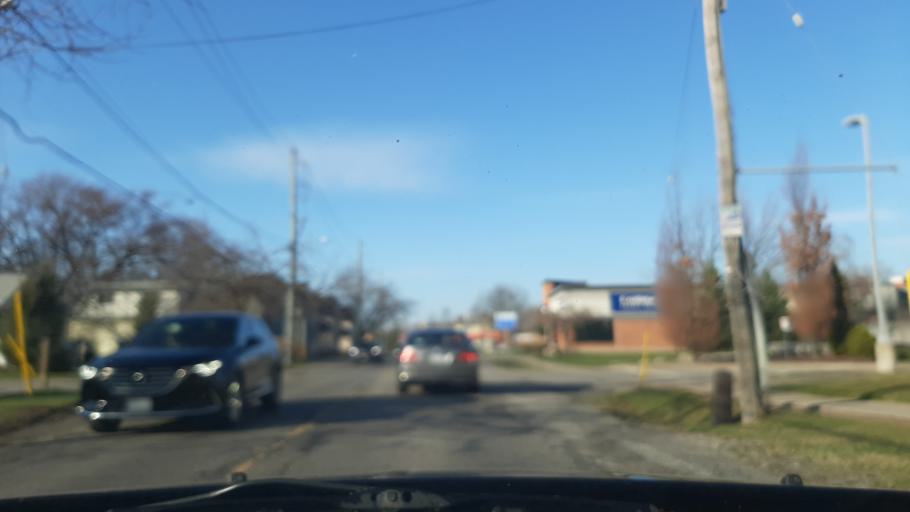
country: CA
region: Ontario
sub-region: Regional Municipality of Niagara
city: St. Catharines
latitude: 43.1944
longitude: -79.2604
